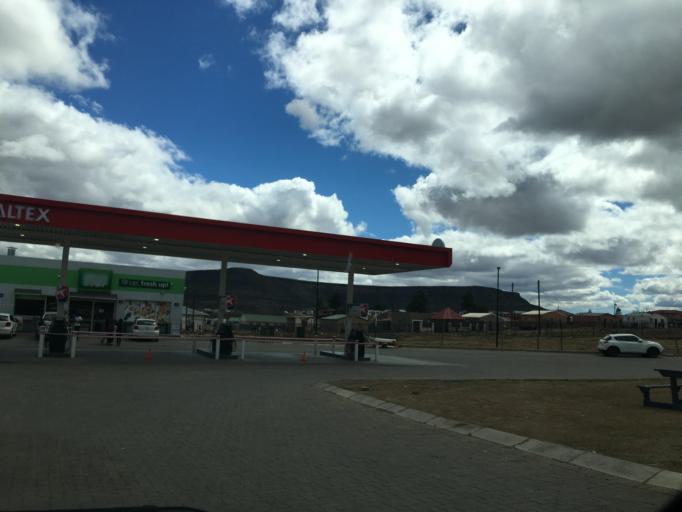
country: ZA
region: Eastern Cape
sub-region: Chris Hani District Municipality
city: Cala
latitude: -31.5269
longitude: 27.6910
